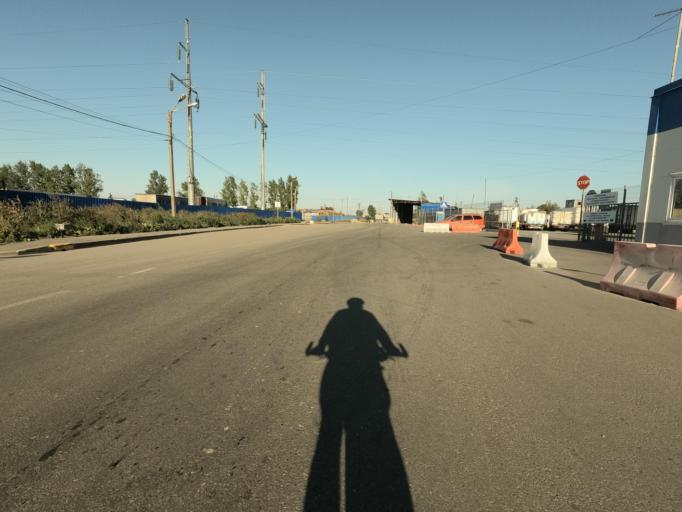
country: RU
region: St.-Petersburg
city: Petro-Slavyanka
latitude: 59.7619
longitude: 30.4763
